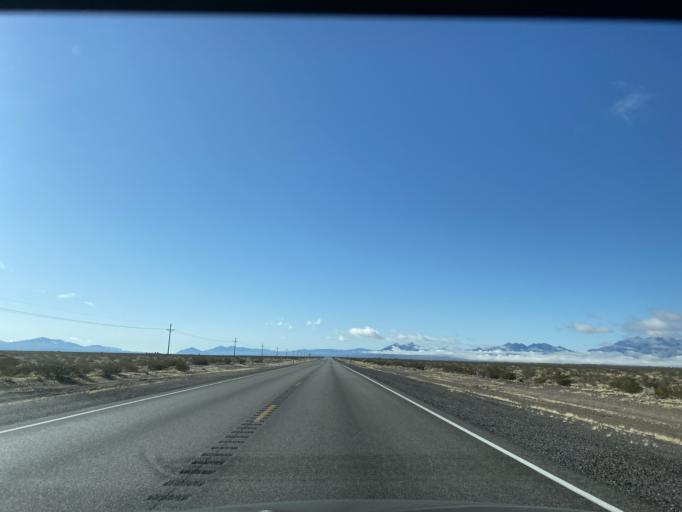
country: US
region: Nevada
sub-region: Nye County
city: Beatty
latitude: 36.5988
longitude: -116.4084
